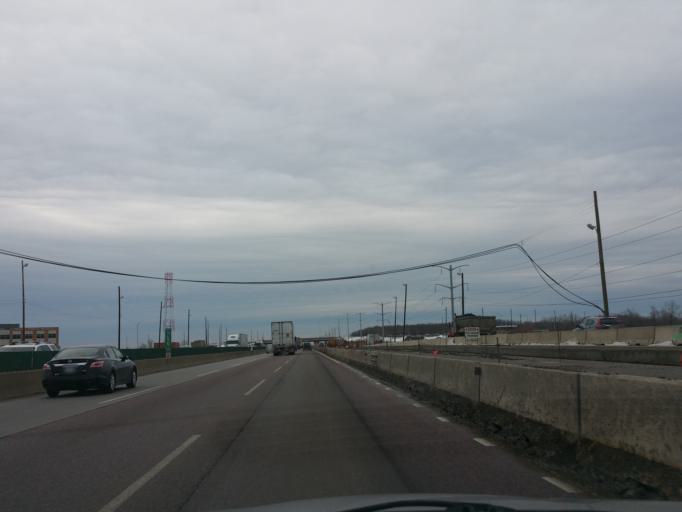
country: US
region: Illinois
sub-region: Cook County
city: Streamwood
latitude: 42.0665
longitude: -88.2028
